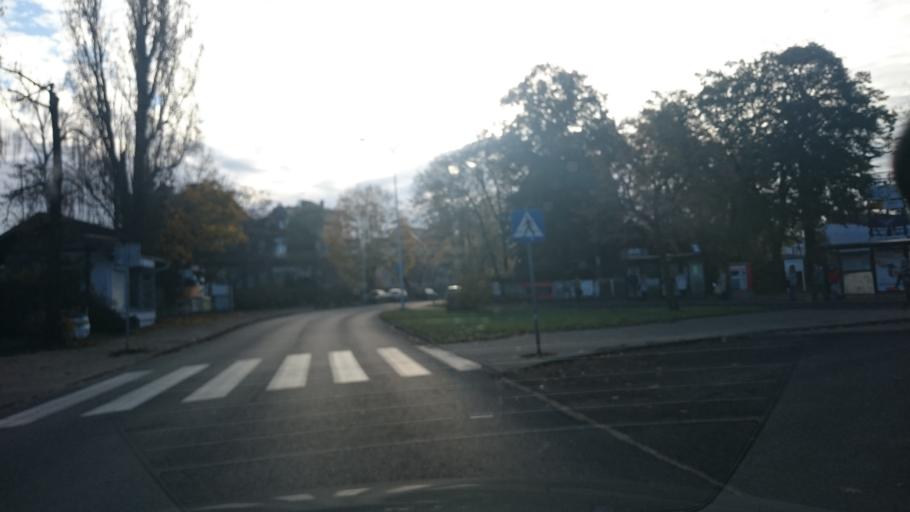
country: PL
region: Pomeranian Voivodeship
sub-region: Sopot
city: Sopot
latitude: 54.4113
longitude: 18.5726
